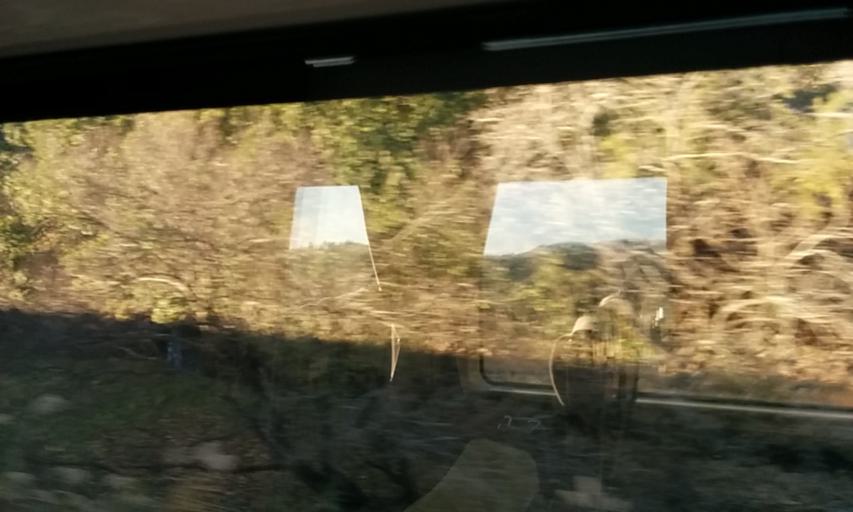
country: JP
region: Gifu
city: Mizunami
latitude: 35.4388
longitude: 137.3669
